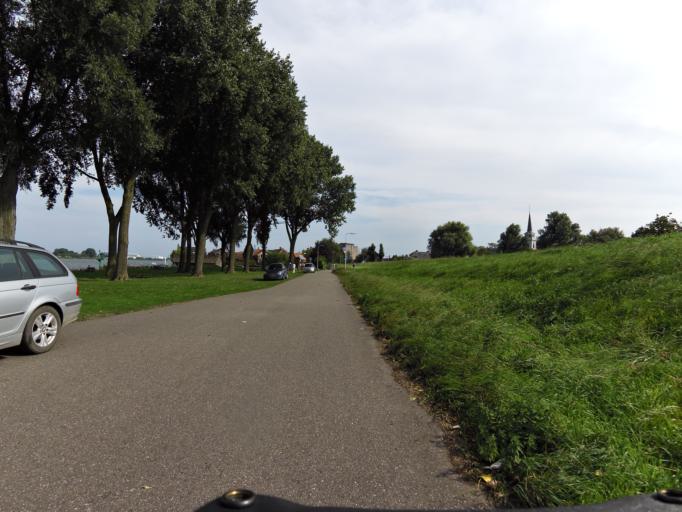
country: NL
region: South Holland
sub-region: Gemeente Zwijndrecht
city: Heerjansdam
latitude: 51.8075
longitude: 4.5745
